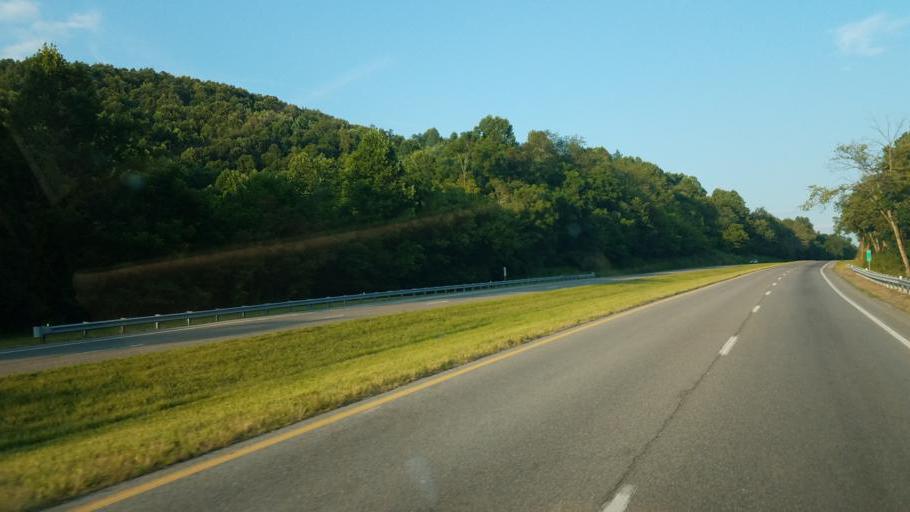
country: US
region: Tennessee
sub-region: Hawkins County
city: Mount Carmel
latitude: 36.6418
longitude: -82.7009
